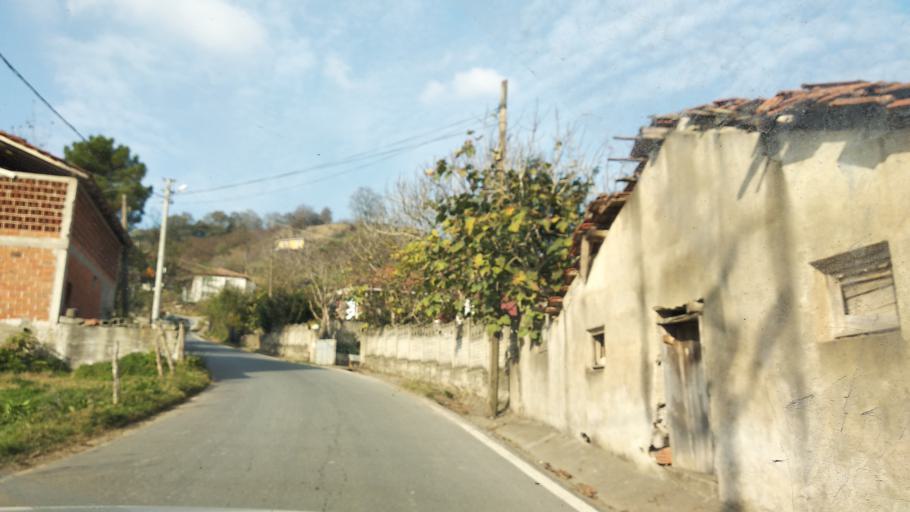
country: TR
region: Sakarya
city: Karasu
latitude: 41.0565
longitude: 30.6268
